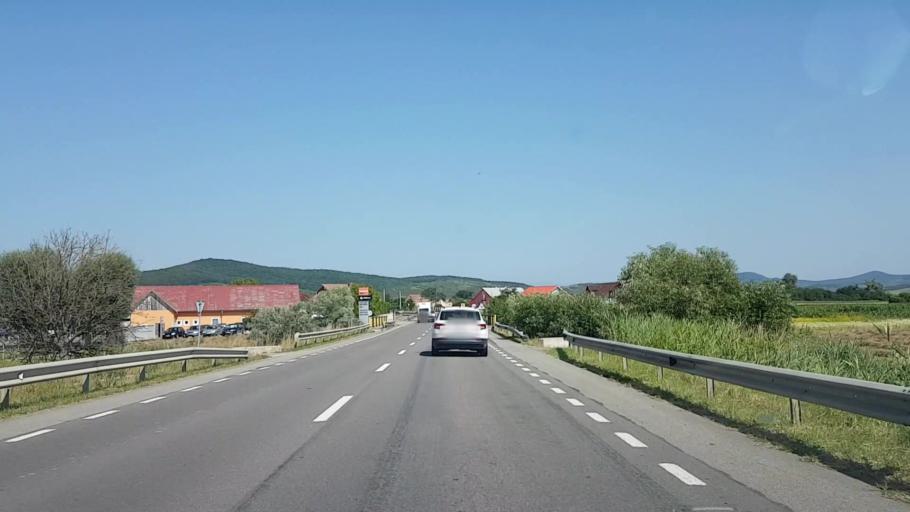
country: RO
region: Bistrita-Nasaud
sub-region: Comuna Sintereag
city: Sintereag
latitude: 47.1793
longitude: 24.2750
